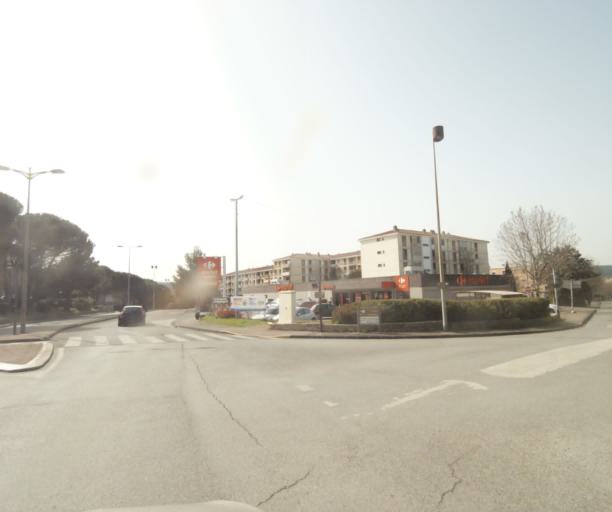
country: FR
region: Provence-Alpes-Cote d'Azur
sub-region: Departement des Bouches-du-Rhone
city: Gardanne
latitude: 43.4543
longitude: 5.4766
